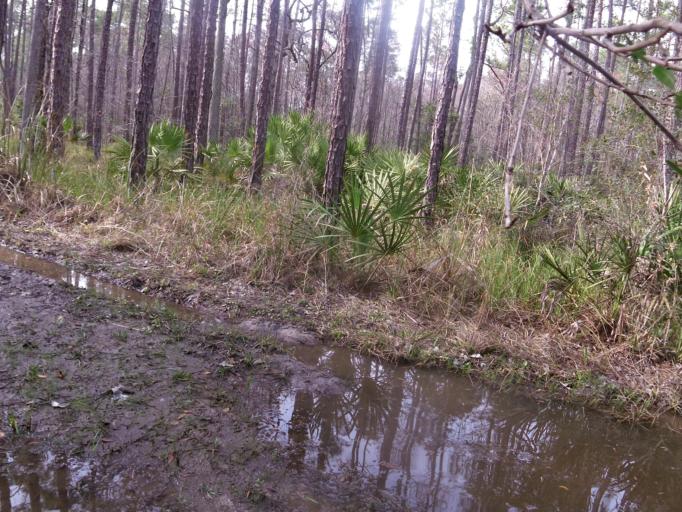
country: US
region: Florida
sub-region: Clay County
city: Middleburg
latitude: 30.1145
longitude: -81.8997
